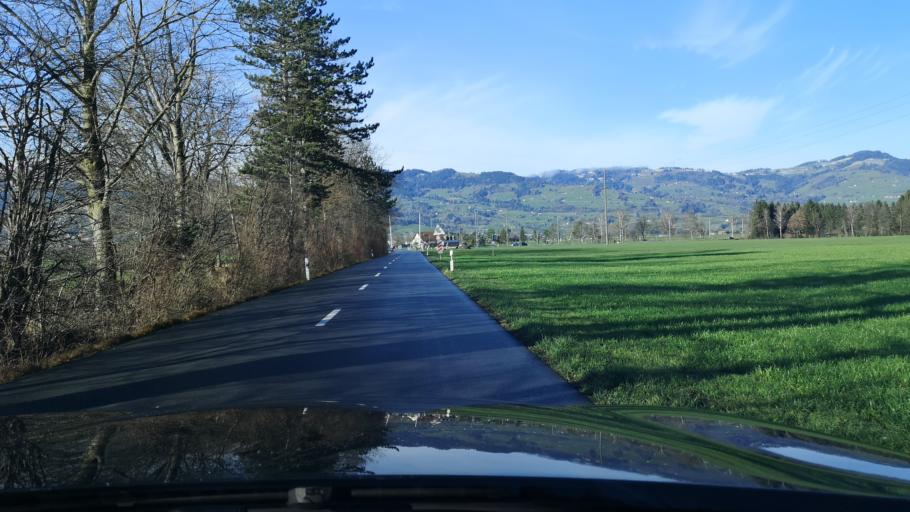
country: CH
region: Saint Gallen
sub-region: Wahlkreis Rheintal
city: Oberriet
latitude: 47.3422
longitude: 9.5688
